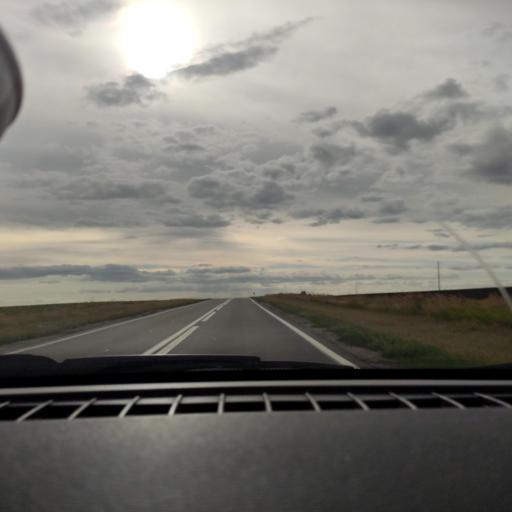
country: RU
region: Samara
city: Georgiyevka
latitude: 53.4168
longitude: 50.8973
